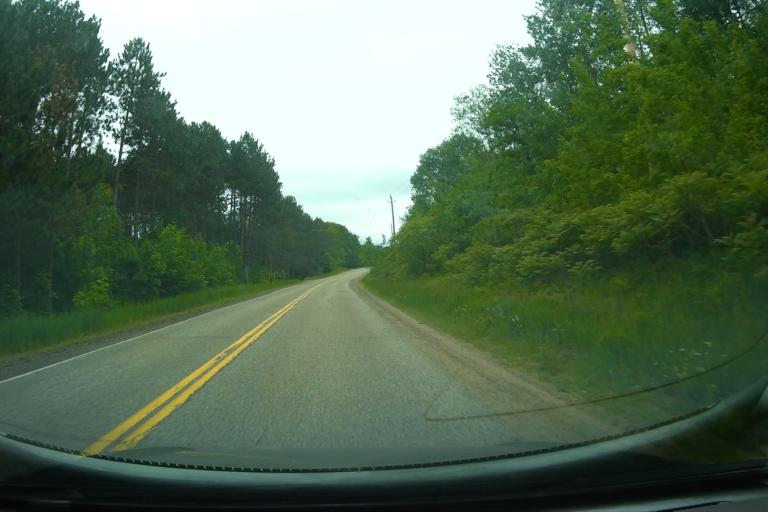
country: CA
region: Ontario
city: Pembroke
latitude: 45.4655
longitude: -77.2283
